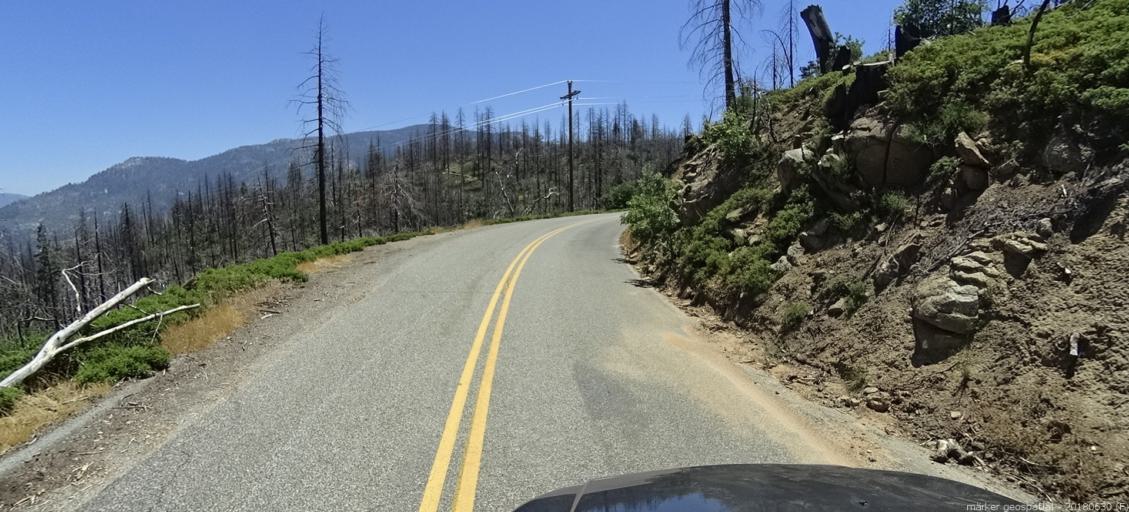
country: US
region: California
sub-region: Fresno County
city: Auberry
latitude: 37.2654
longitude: -119.3517
